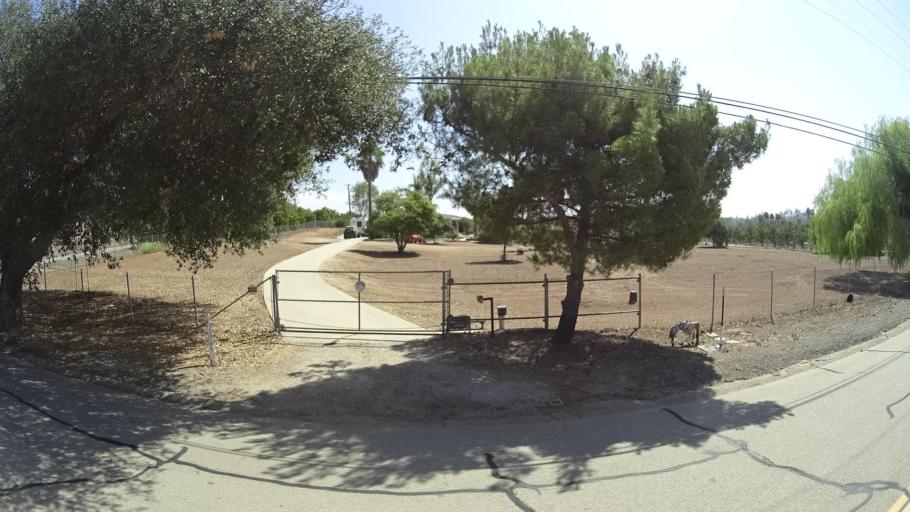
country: US
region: California
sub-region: San Diego County
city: Valley Center
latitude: 33.2890
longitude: -117.0325
